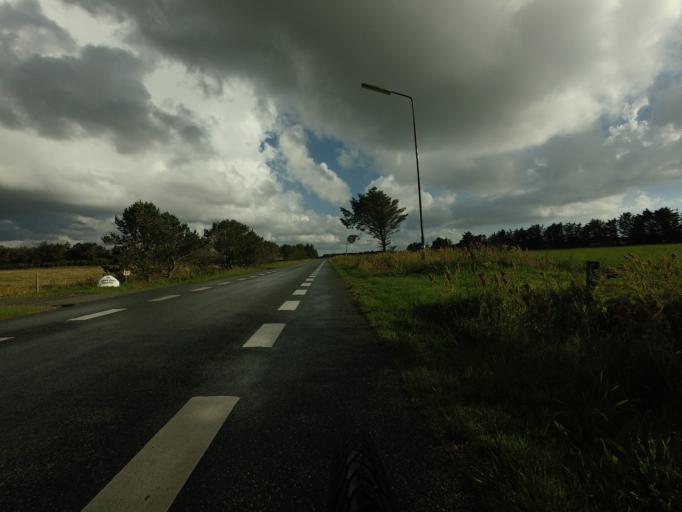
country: DK
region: North Denmark
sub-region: Hjorring Kommune
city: Hjorring
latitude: 57.4604
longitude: 9.7970
